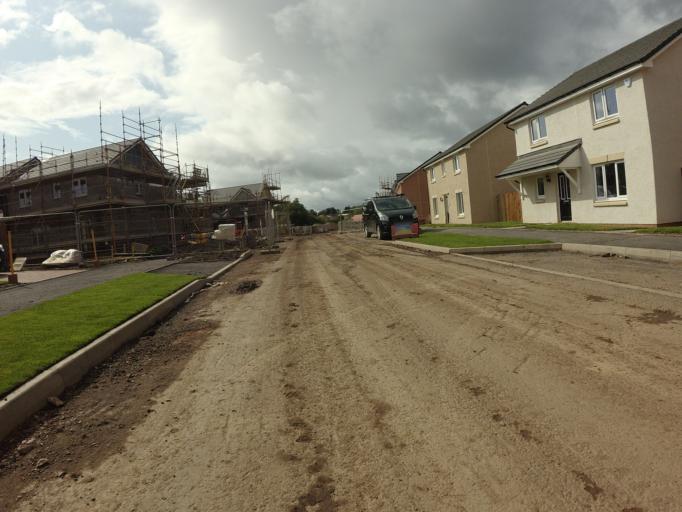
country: GB
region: Scotland
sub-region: East Lothian
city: Musselburgh
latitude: 55.9383
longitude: -3.0287
